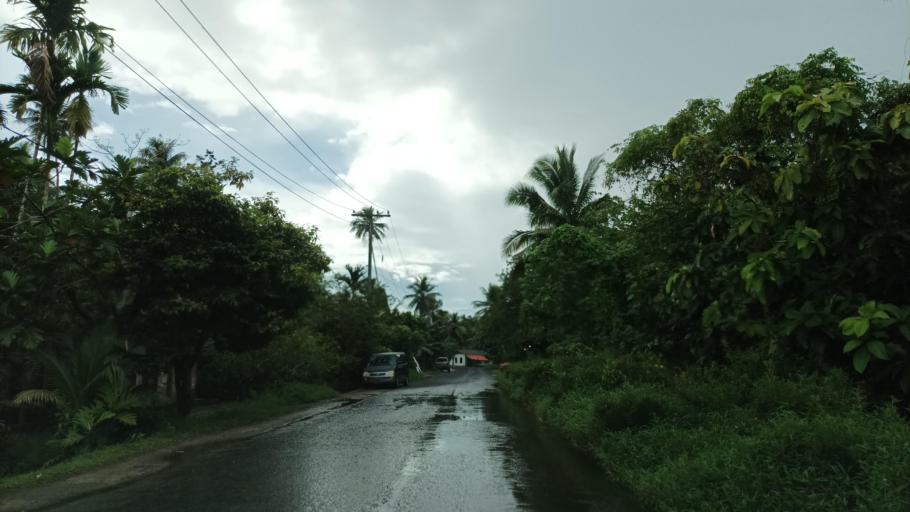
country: FM
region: Pohnpei
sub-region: Kolonia Municipality
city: Kolonia
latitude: 6.9283
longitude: 158.2792
